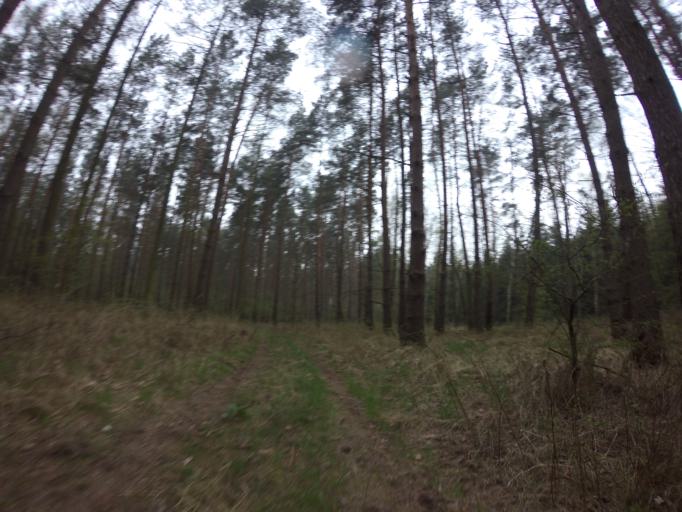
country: PL
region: West Pomeranian Voivodeship
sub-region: Powiat choszczenski
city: Recz
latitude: 53.1846
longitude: 15.5262
